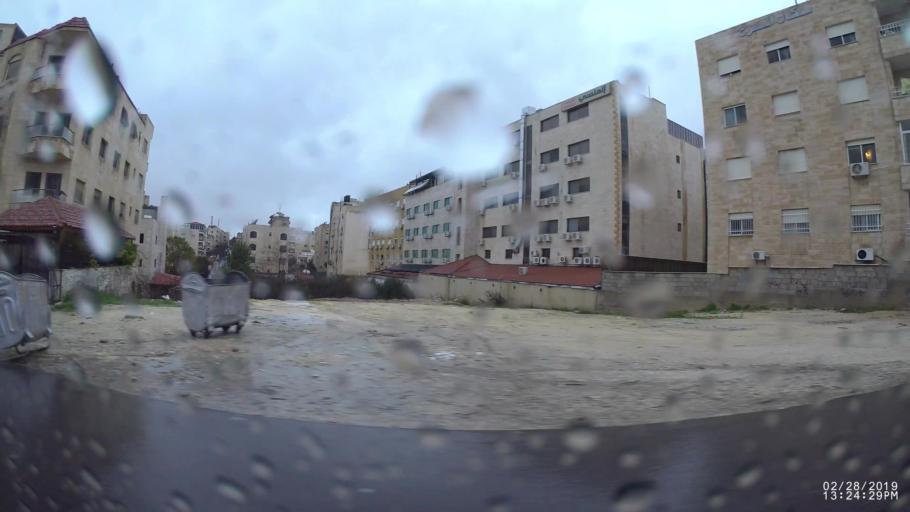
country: JO
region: Amman
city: Al Jubayhah
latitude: 32.0170
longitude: 35.8803
